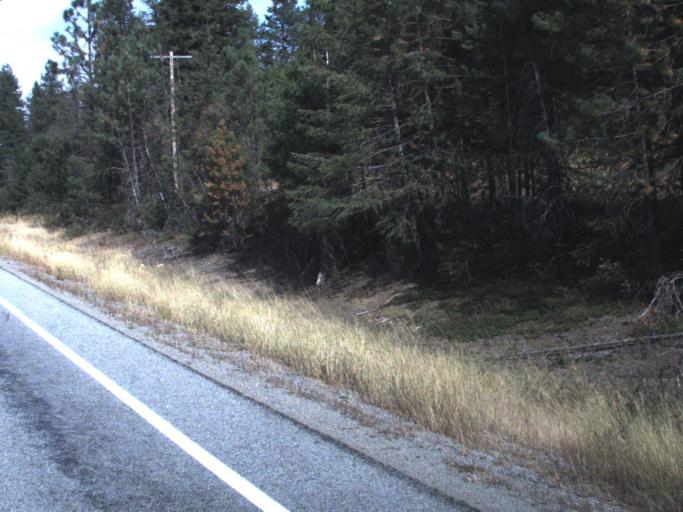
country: US
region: Washington
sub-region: Pend Oreille County
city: Newport
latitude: 48.2300
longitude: -117.2893
